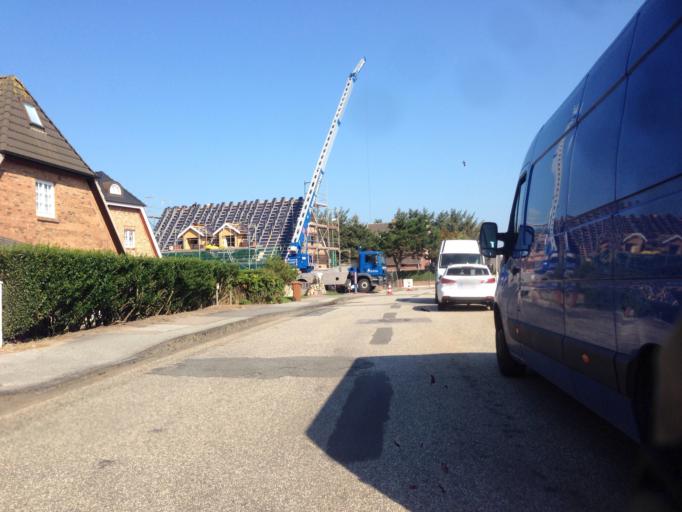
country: DE
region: Schleswig-Holstein
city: Westerland
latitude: 54.9157
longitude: 8.3089
